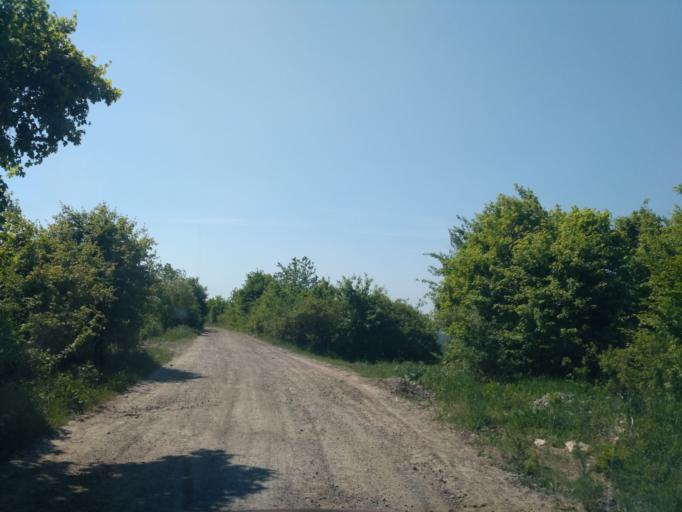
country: SK
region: Kosicky
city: Kosice
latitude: 48.8334
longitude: 21.4517
